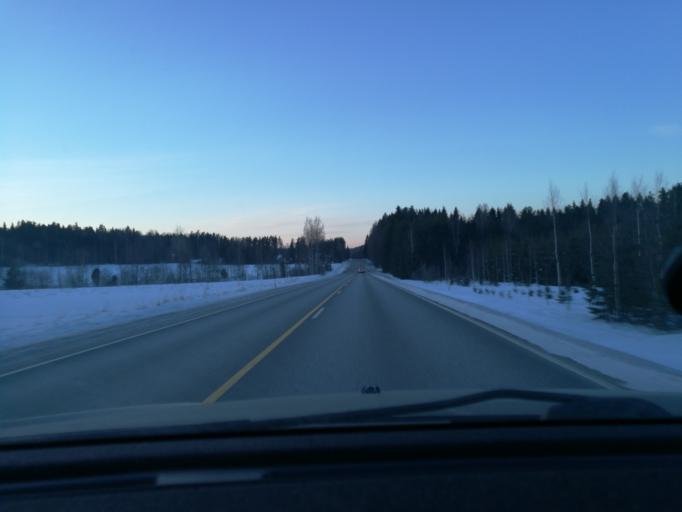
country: FI
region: Uusimaa
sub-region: Helsinki
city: Vihti
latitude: 60.4206
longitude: 24.4399
